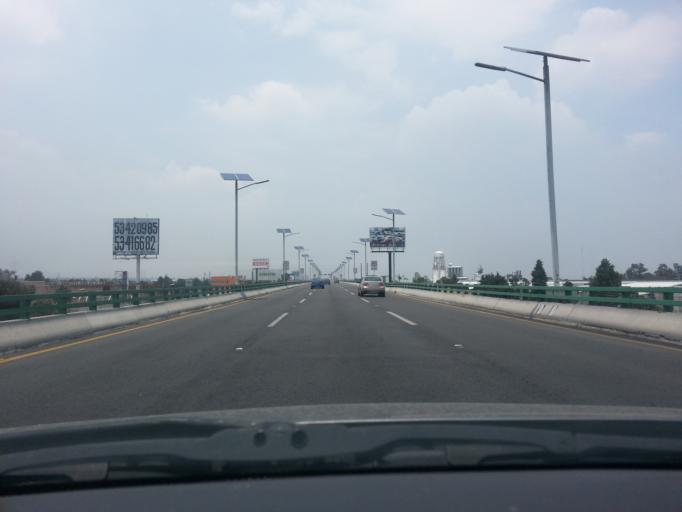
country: MX
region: Mexico
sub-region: Tultitlan
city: Buenavista
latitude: 19.6104
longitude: -99.1900
